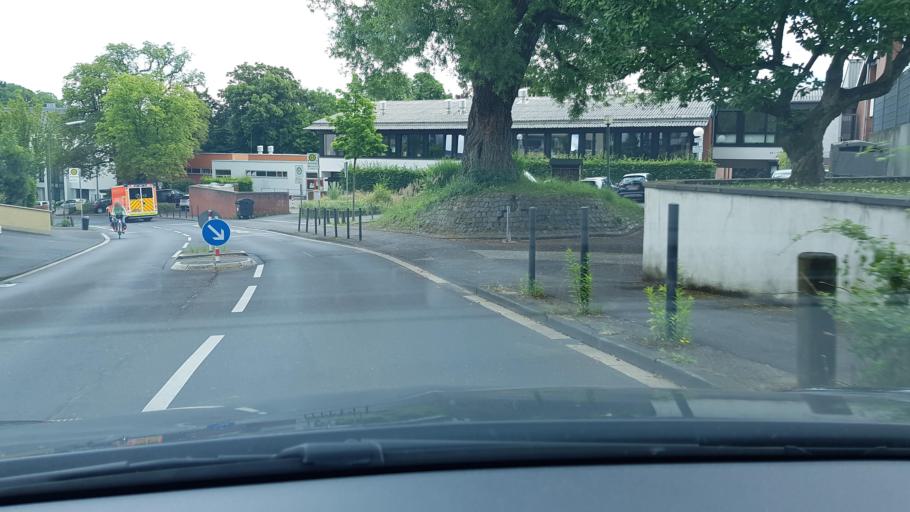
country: DE
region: North Rhine-Westphalia
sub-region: Regierungsbezirk Koln
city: Konigswinter
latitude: 50.6835
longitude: 7.1458
